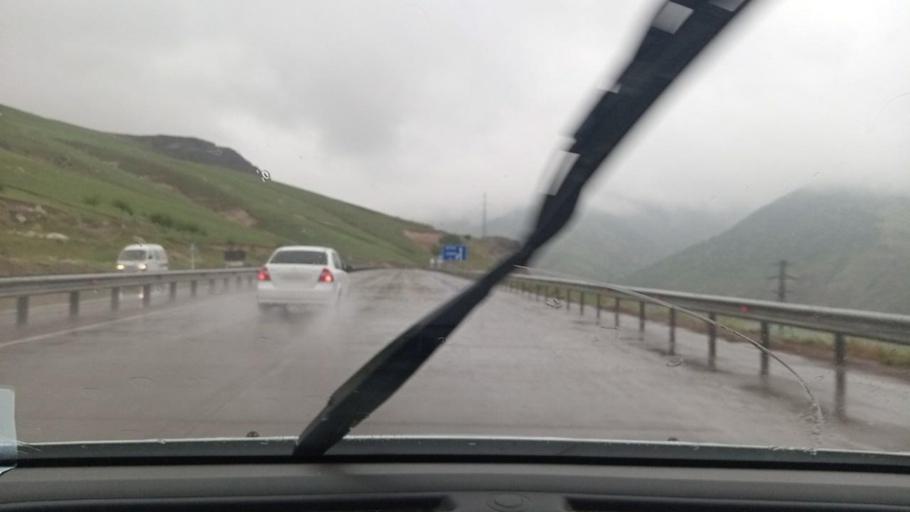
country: UZ
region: Toshkent
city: Angren
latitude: 41.0745
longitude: 70.2646
